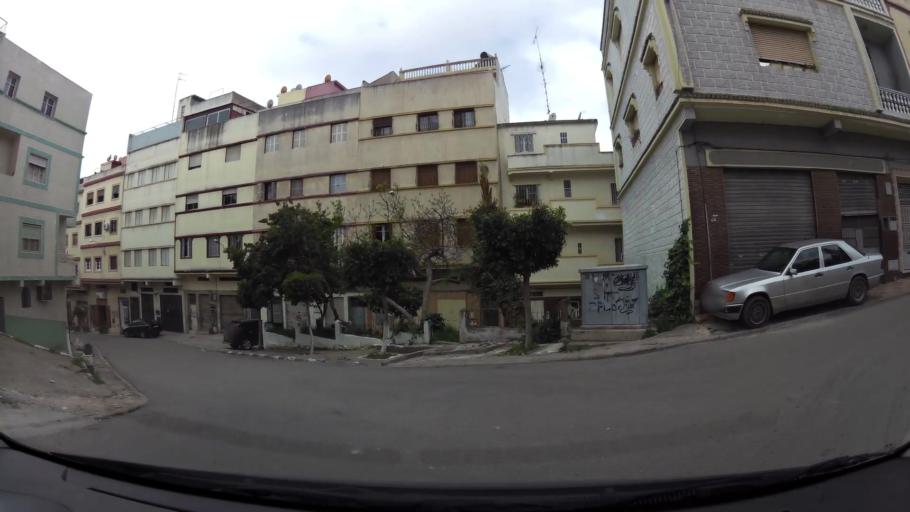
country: MA
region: Tanger-Tetouan
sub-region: Tanger-Assilah
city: Tangier
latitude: 35.7726
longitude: -5.8205
